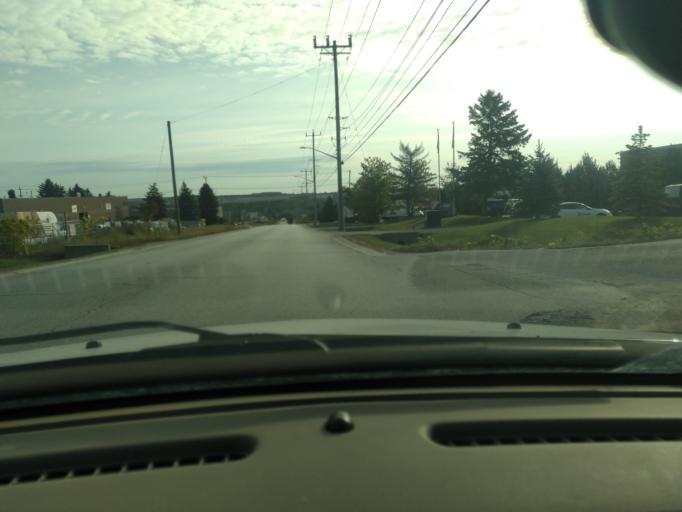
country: CA
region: Ontario
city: Innisfil
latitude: 44.3338
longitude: -79.6706
